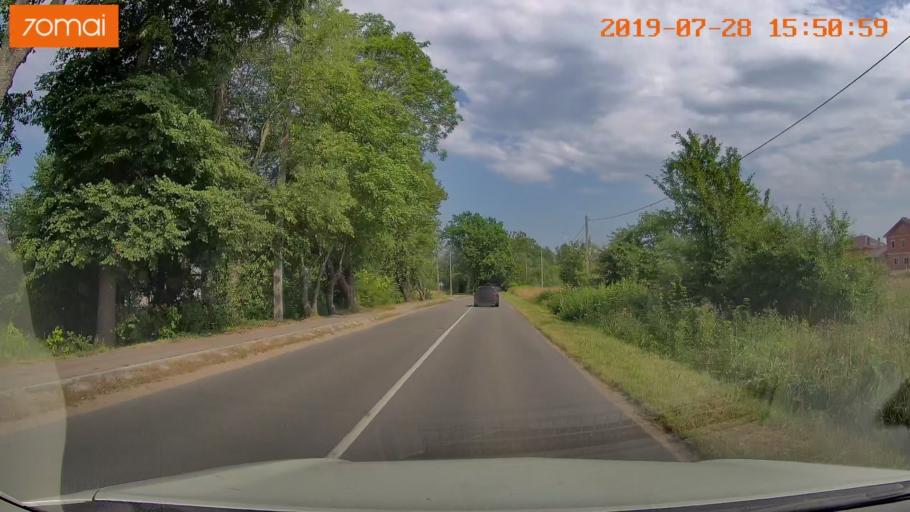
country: RU
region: Kaliningrad
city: Otradnoye
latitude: 54.9417
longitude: 20.0986
